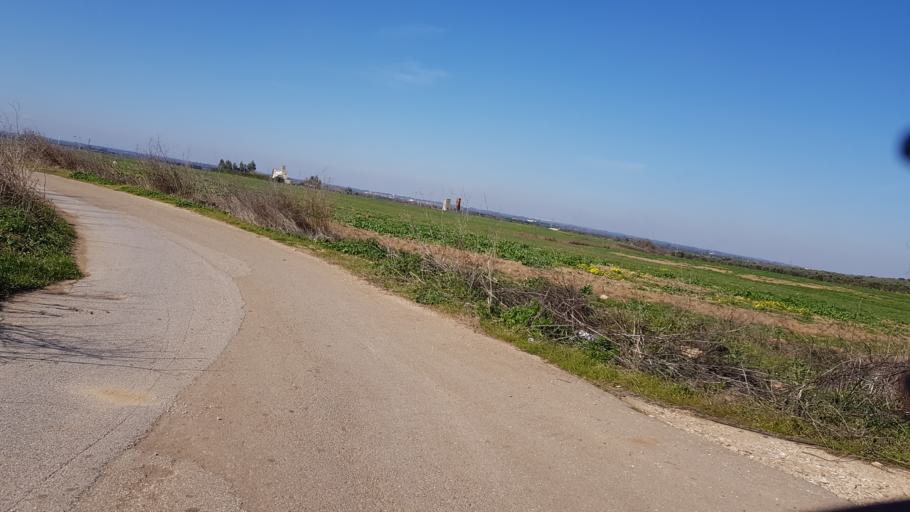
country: IT
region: Apulia
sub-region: Provincia di Brindisi
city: Mesagne
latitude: 40.6217
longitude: 17.8277
